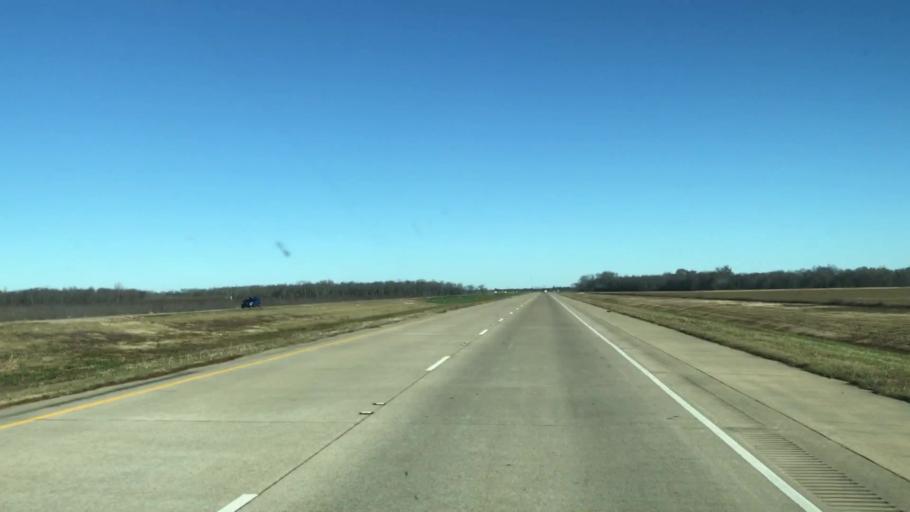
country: US
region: Louisiana
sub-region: Caddo Parish
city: Blanchard
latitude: 32.6342
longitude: -93.8378
